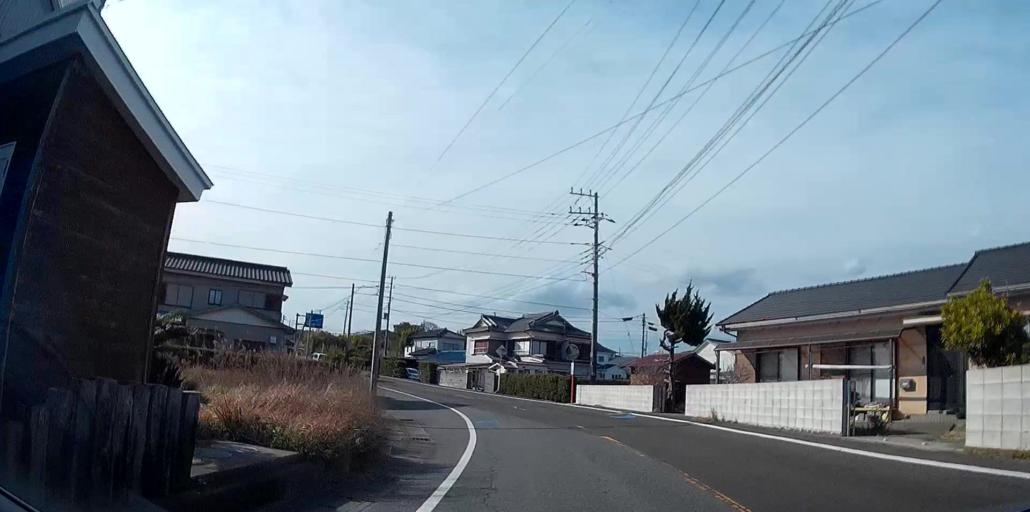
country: JP
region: Chiba
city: Tateyama
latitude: 34.9641
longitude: 139.9592
